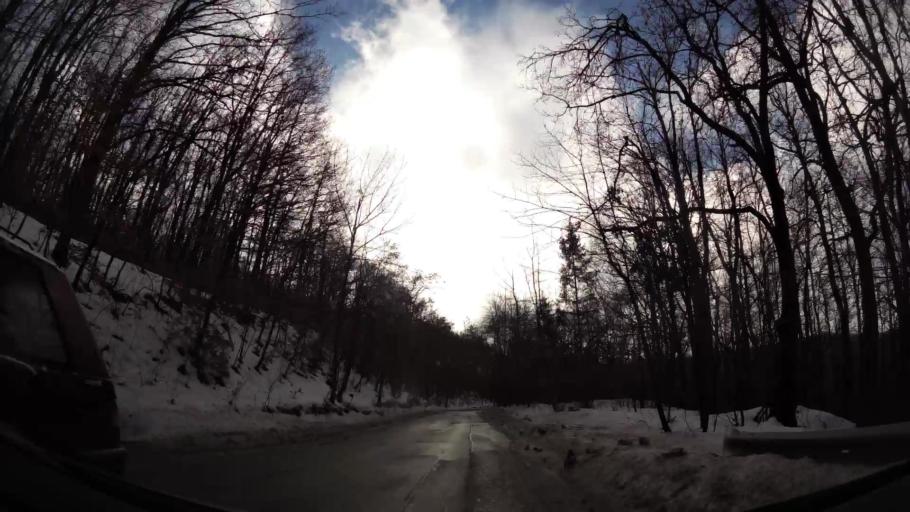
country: BG
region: Sofiya
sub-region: Obshtina Bozhurishte
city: Bozhurishte
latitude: 42.6366
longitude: 23.2218
